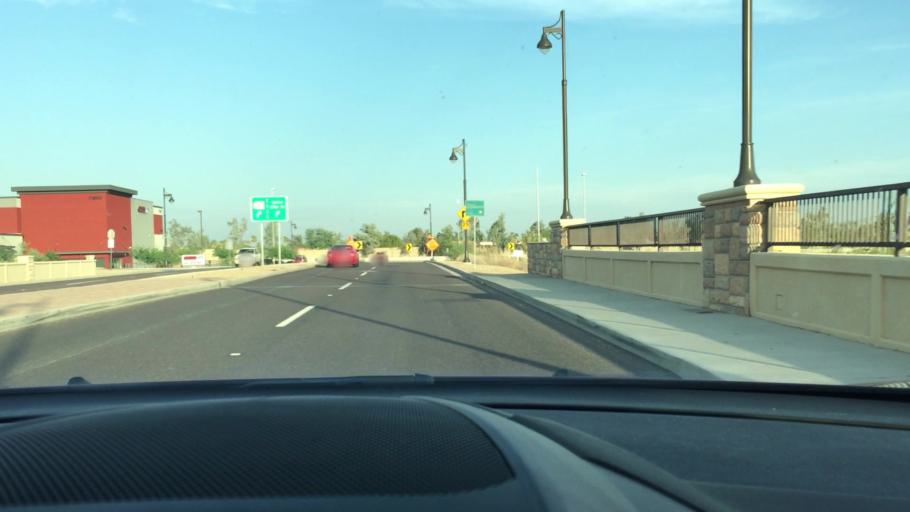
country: US
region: Arizona
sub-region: Maricopa County
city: Sun City
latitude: 33.6663
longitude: -112.2308
